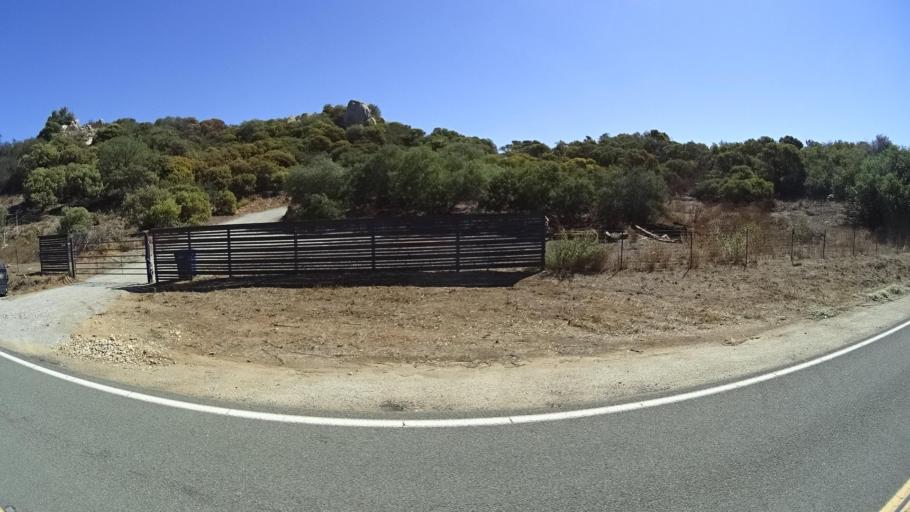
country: US
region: California
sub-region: San Diego County
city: Descanso
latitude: 32.7573
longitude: -116.6759
